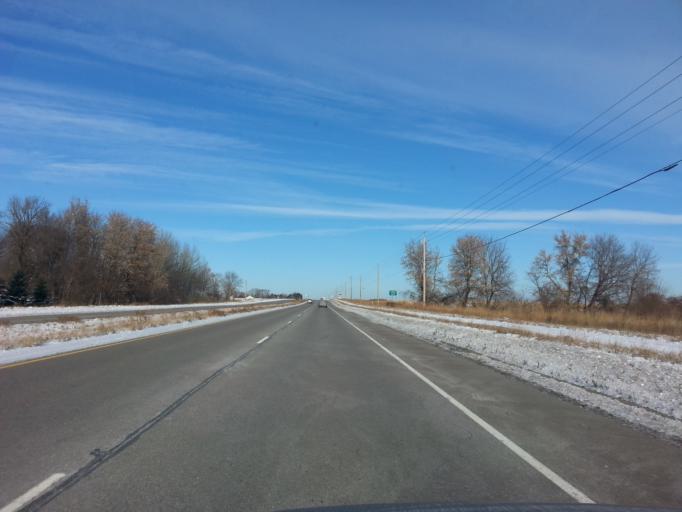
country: US
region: Minnesota
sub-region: Scott County
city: Shakopee
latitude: 44.7637
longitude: -93.4695
